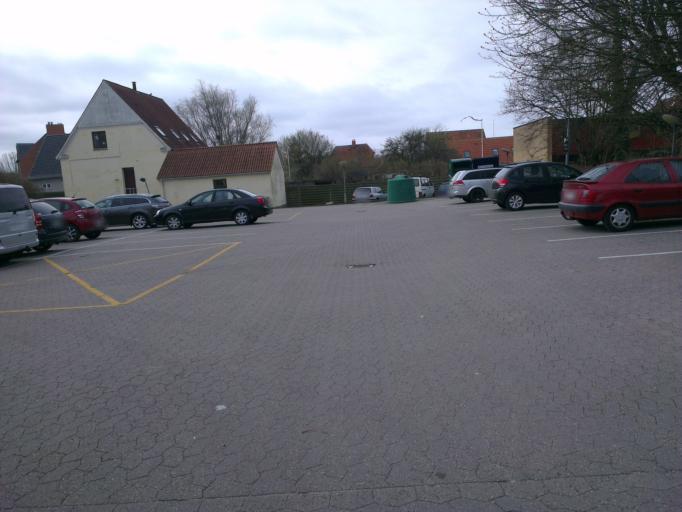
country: PL
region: Lower Silesian Voivodeship
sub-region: Powiat olesnicki
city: Dziadowa Kloda
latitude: 51.2402
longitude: 17.7268
